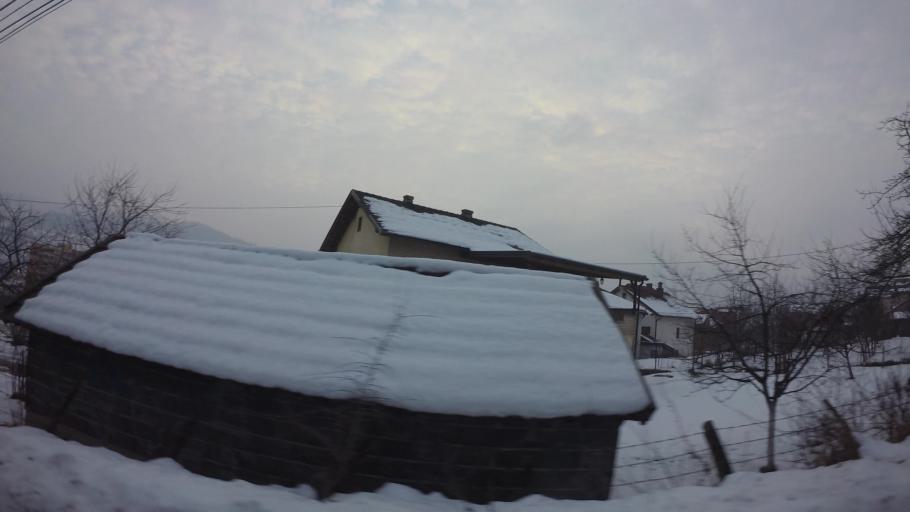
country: BA
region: Federation of Bosnia and Herzegovina
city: Vogosca
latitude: 43.9039
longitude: 18.3527
